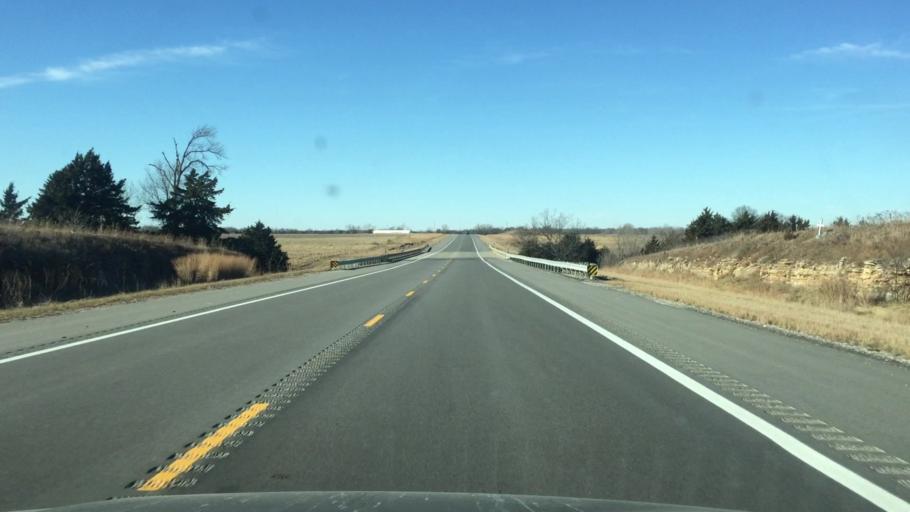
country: US
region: Kansas
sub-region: Franklin County
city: Ottawa
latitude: 38.4665
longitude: -95.2581
